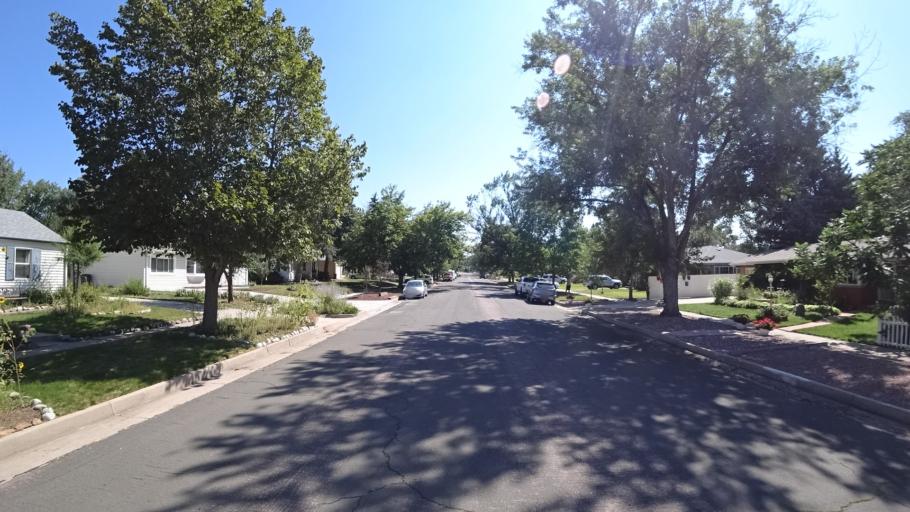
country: US
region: Colorado
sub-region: El Paso County
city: Colorado Springs
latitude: 38.8639
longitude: -104.8047
